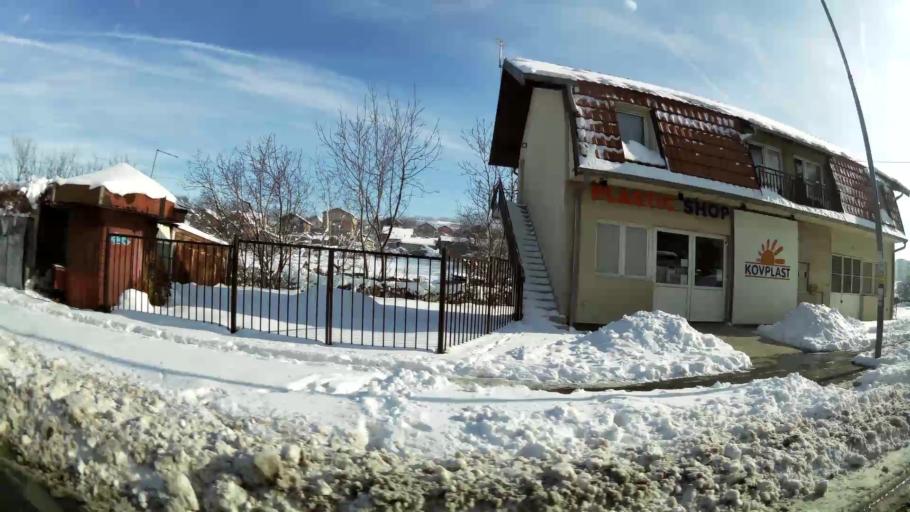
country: RS
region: Central Serbia
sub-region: Belgrade
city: Palilula
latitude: 44.8070
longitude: 20.5246
